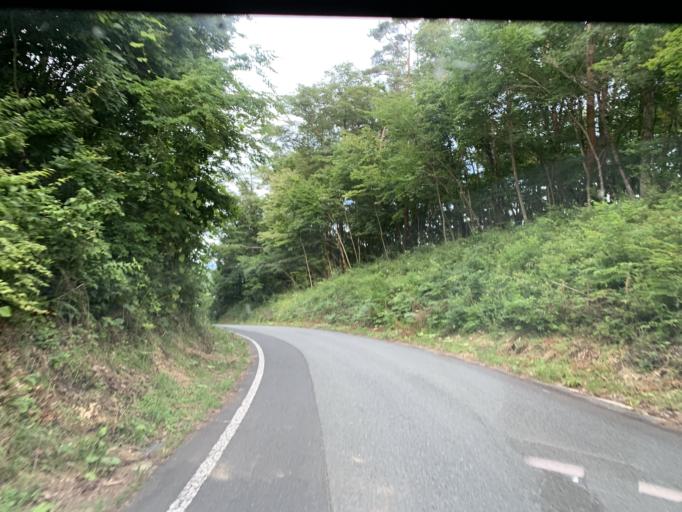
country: JP
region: Iwate
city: Ichinoseki
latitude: 38.9127
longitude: 141.0430
